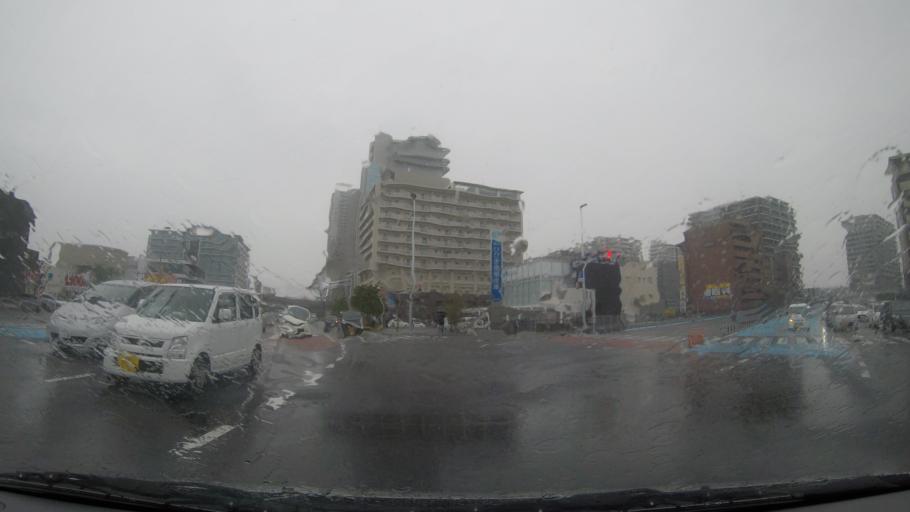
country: JP
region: Fukuoka
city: Fukuoka-shi
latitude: 33.6471
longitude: 130.4409
